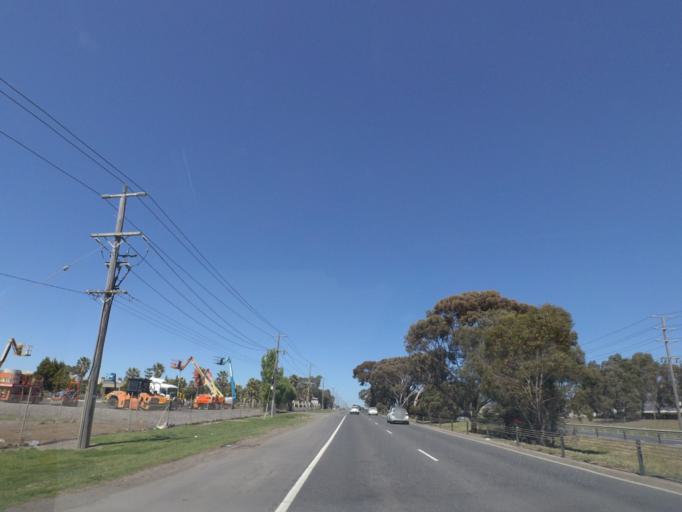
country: AU
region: Victoria
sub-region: Hume
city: Roxburgh Park
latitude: -37.6229
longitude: 144.9483
